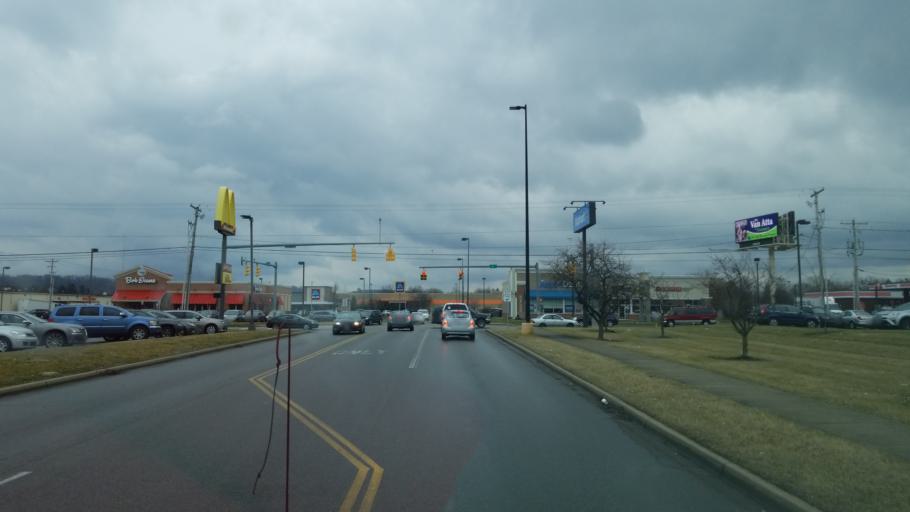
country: US
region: Ohio
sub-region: Licking County
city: Newark
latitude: 40.0839
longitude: -82.4286
